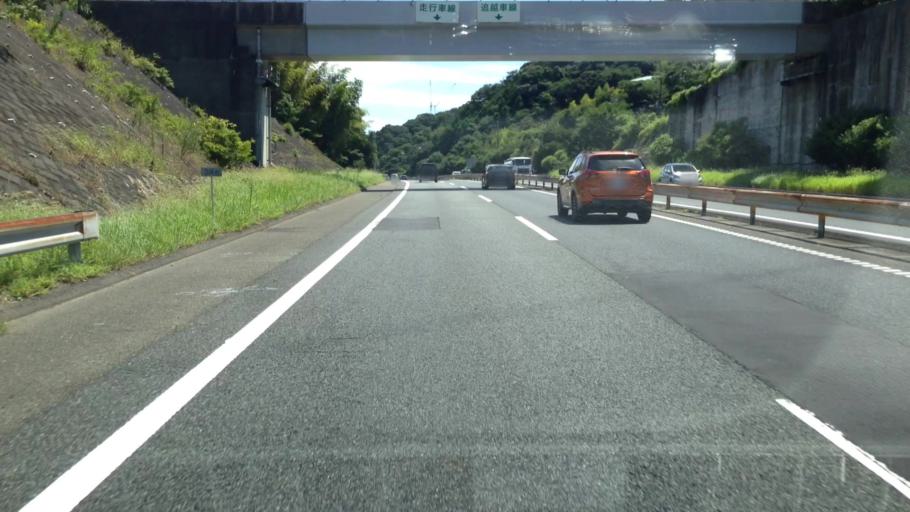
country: JP
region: Kanagawa
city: Yokosuka
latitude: 35.2593
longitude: 139.6341
